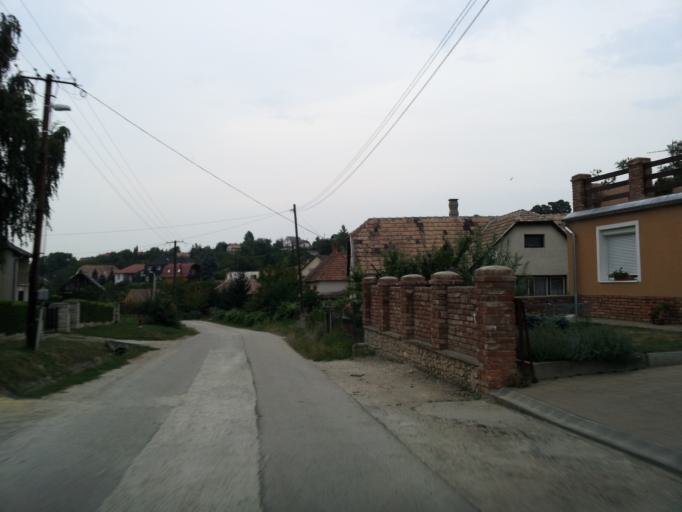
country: HU
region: Vas
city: Sarvar
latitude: 47.2417
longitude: 16.9676
